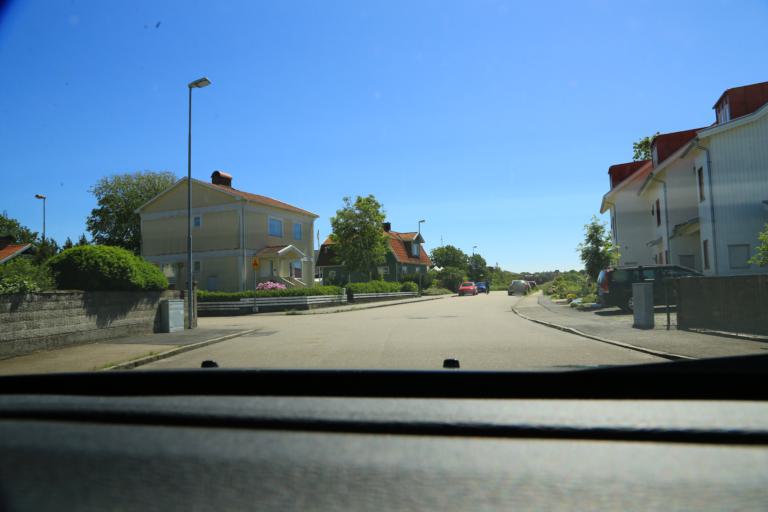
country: SE
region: Halland
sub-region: Varbergs Kommun
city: Varberg
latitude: 57.1142
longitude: 12.2533
